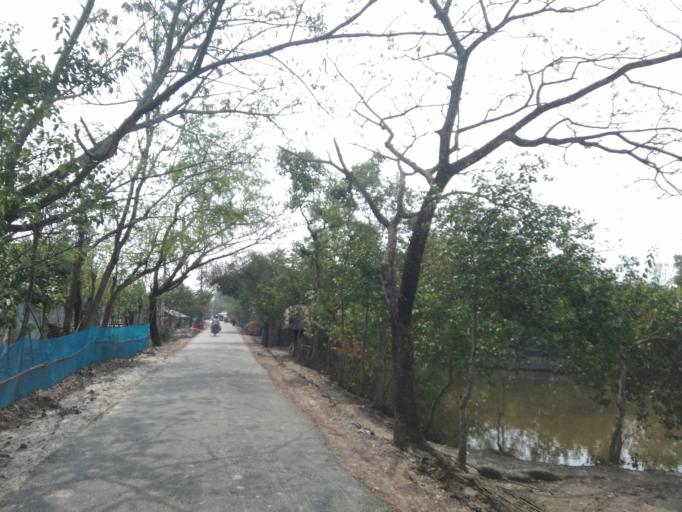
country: IN
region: West Bengal
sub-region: North 24 Parganas
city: Gosaba
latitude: 22.2662
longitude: 89.2180
